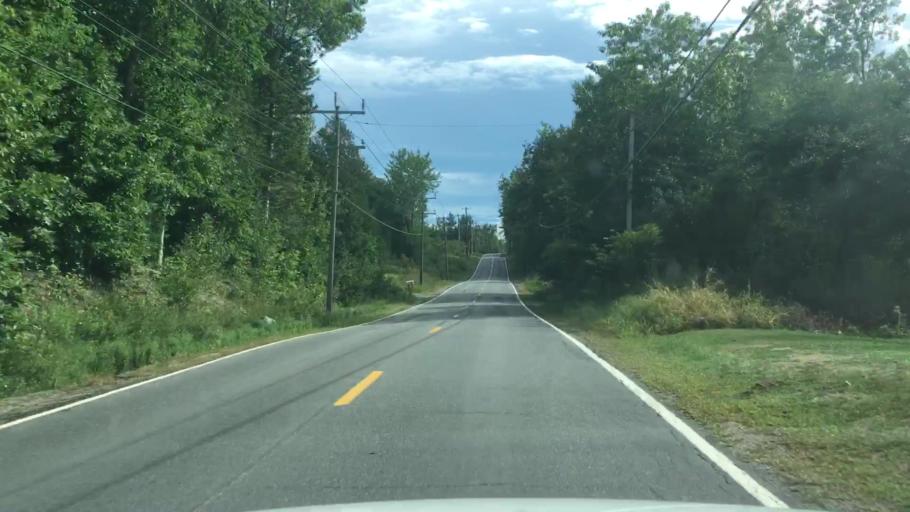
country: US
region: Maine
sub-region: Hancock County
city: Ellsworth
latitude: 44.4919
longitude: -68.4202
